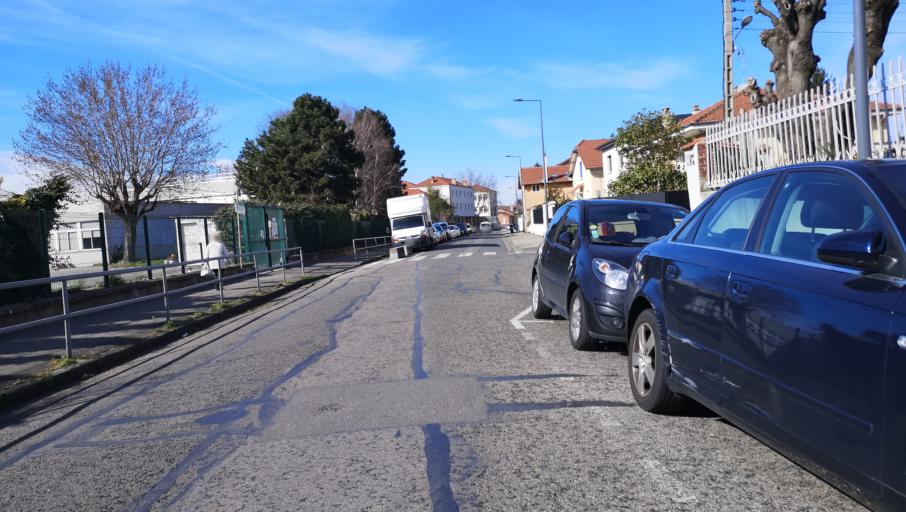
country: FR
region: Rhone-Alpes
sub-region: Departement du Rhone
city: Villeurbanne
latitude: 45.7688
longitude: 4.8995
